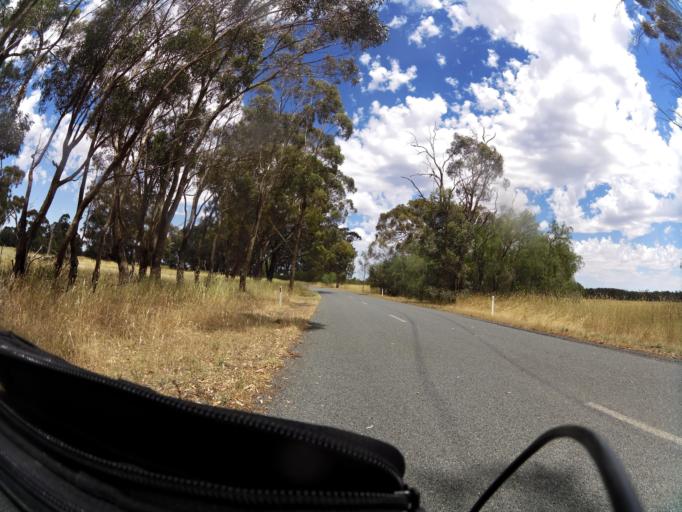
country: AU
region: Victoria
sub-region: Greater Shepparton
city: Shepparton
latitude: -36.6549
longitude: 145.2012
